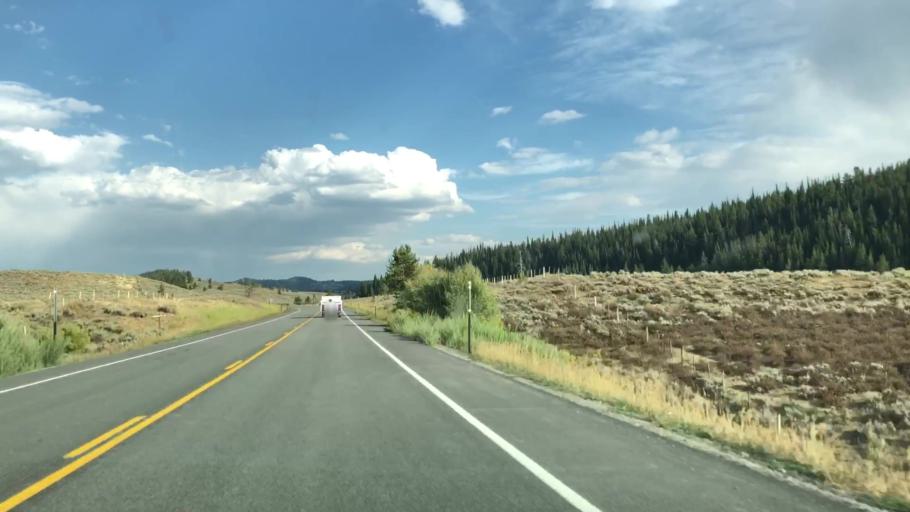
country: US
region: Wyoming
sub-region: Teton County
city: Hoback
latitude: 43.1530
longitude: -110.2938
